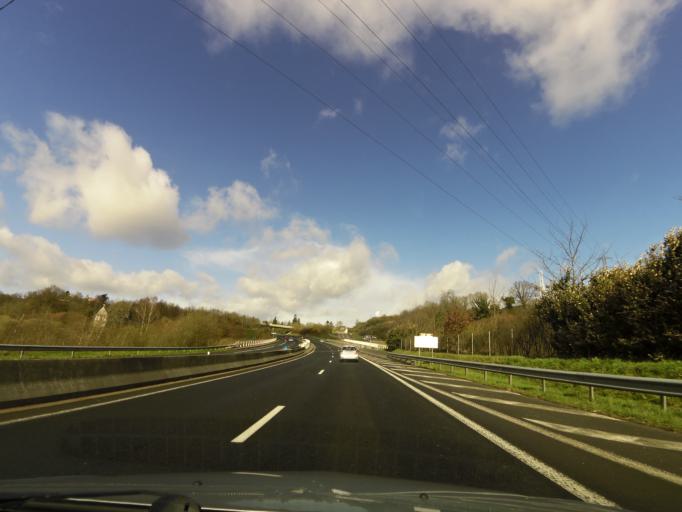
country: FR
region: Lower Normandy
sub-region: Departement de la Manche
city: Agneaux
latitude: 49.1093
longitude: -1.1204
